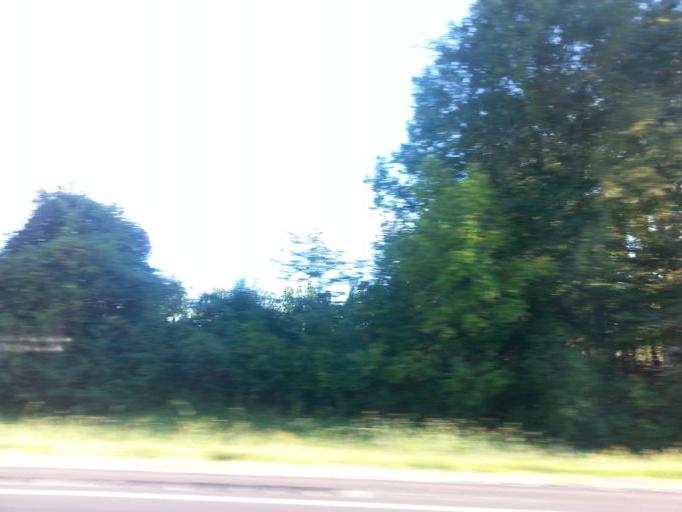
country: US
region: Alabama
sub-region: Lauderdale County
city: Killen
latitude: 34.8594
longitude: -87.4922
